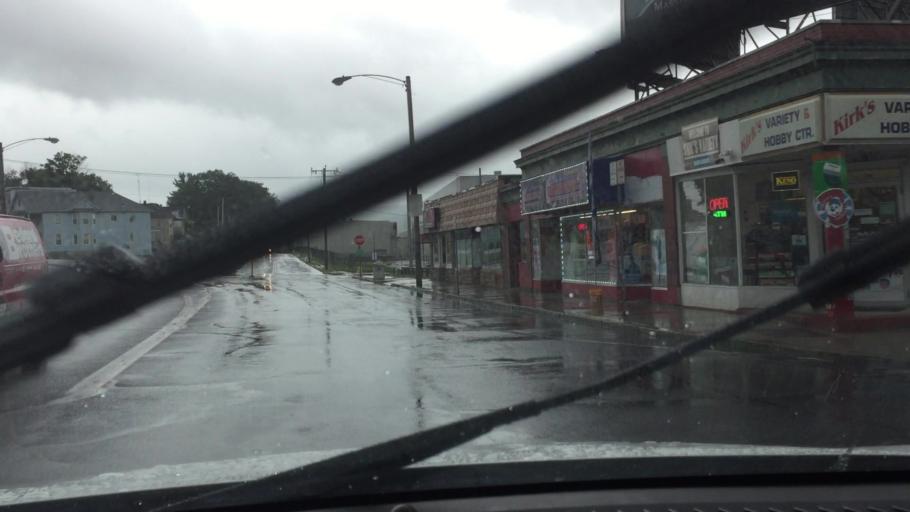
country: US
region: Massachusetts
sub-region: Berkshire County
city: Pittsfield
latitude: 42.4565
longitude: -73.2349
